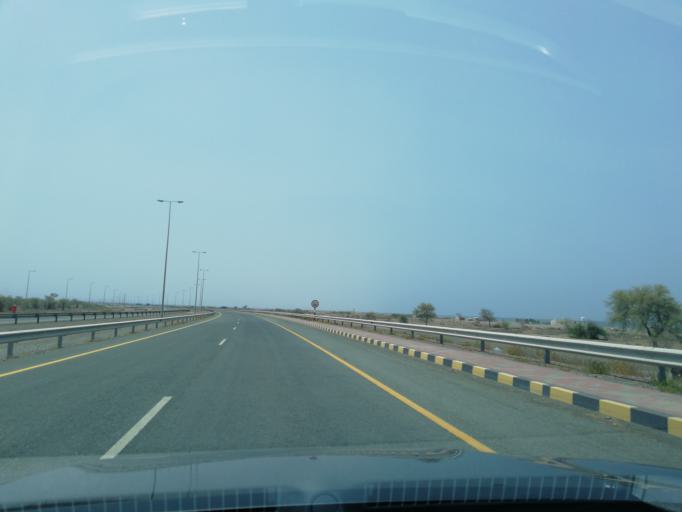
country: OM
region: Al Batinah
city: Shinas
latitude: 24.6594
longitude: 56.5103
